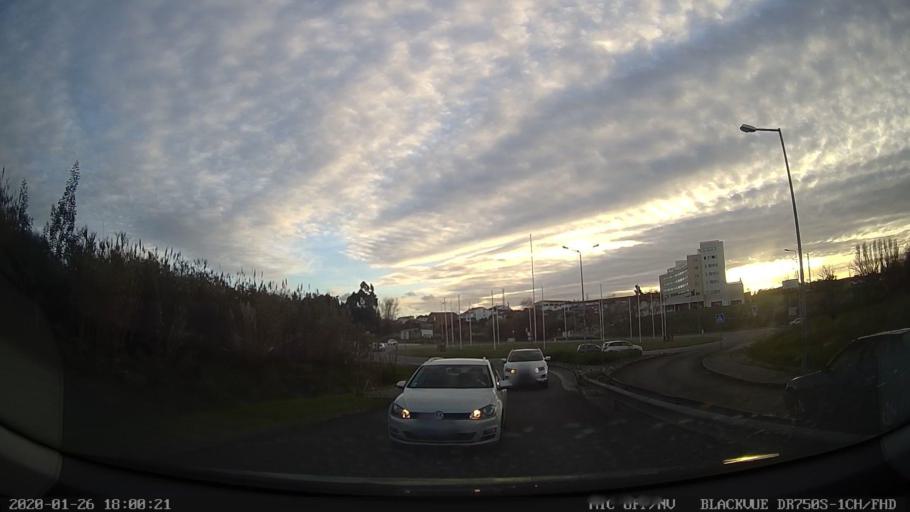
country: PT
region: Aveiro
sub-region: Aveiro
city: Aveiro
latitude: 40.6356
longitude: -8.6345
